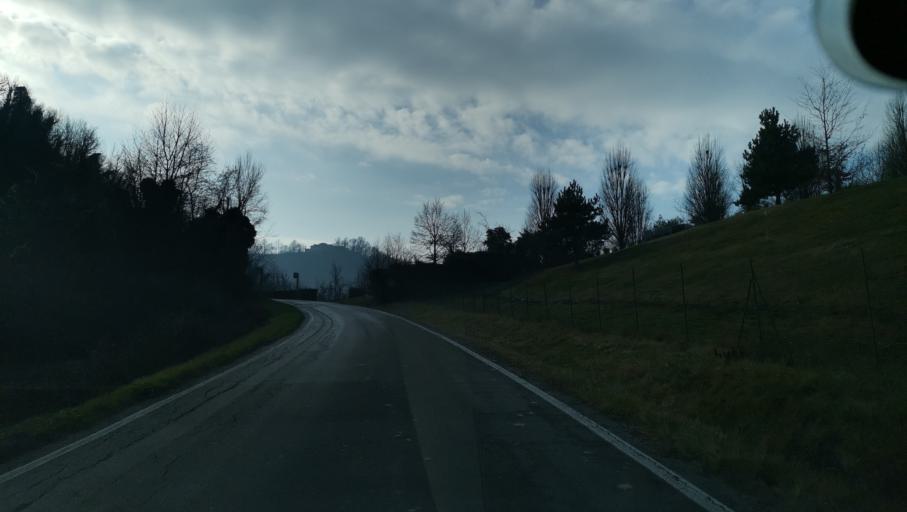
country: IT
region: Piedmont
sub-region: Provincia di Torino
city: Sciolze
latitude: 45.1001
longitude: 7.8906
